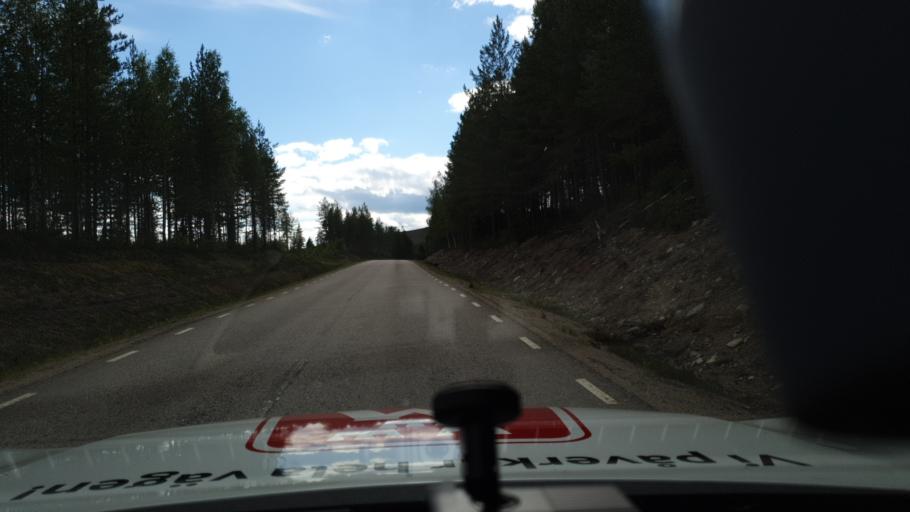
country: NO
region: Hedmark
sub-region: Trysil
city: Innbygda
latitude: 61.0212
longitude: 12.5421
